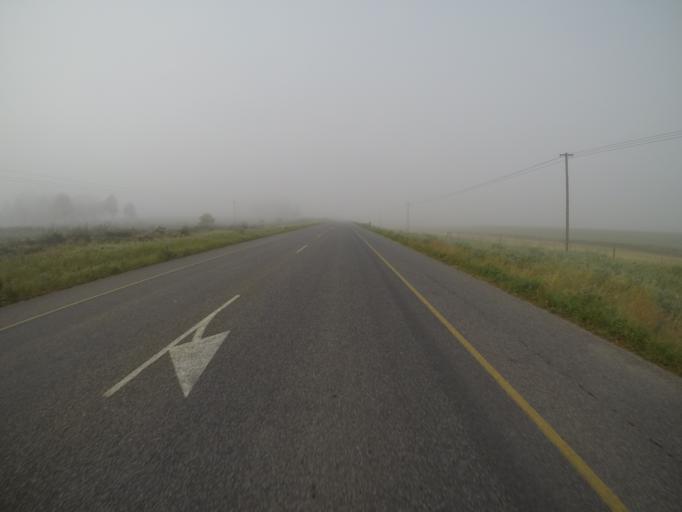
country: ZA
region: Western Cape
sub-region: City of Cape Town
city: Kraaifontein
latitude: -33.6826
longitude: 18.7055
